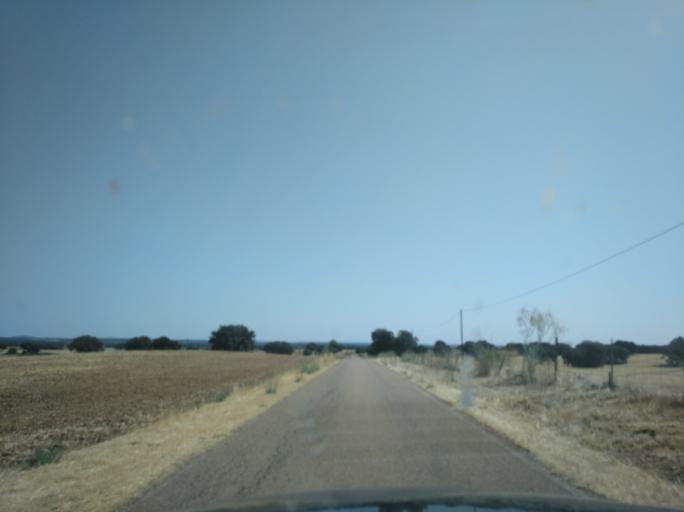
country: PT
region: Portalegre
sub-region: Campo Maior
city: Campo Maior
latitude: 39.0331
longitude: -6.9956
